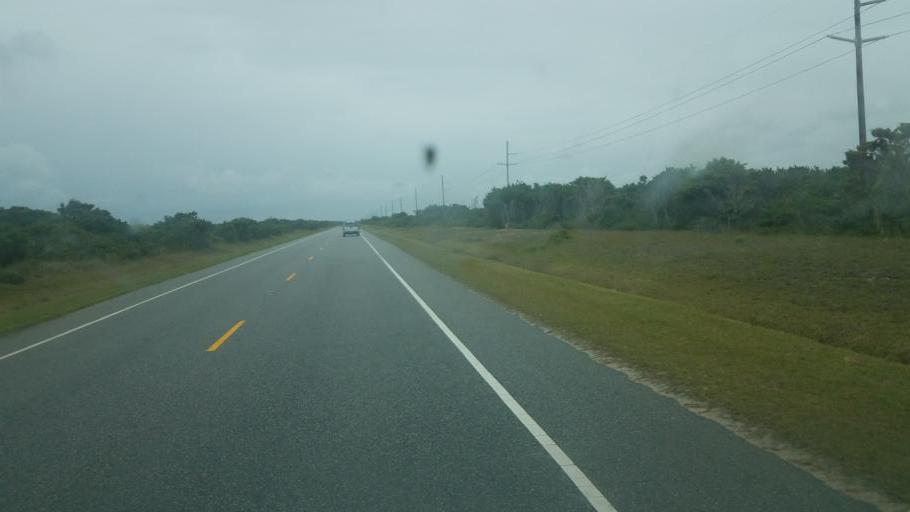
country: US
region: North Carolina
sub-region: Dare County
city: Buxton
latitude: 35.4384
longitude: -75.4861
